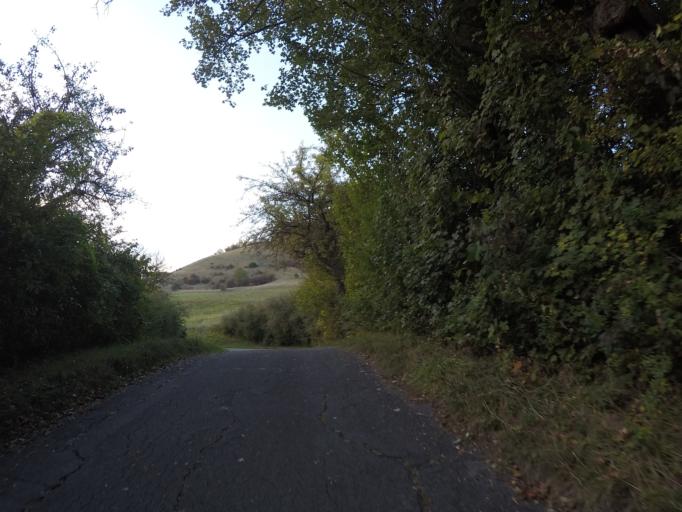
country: DE
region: Baden-Wuerttemberg
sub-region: Tuebingen Region
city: Eningen unter Achalm
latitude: 48.4897
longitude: 9.2487
